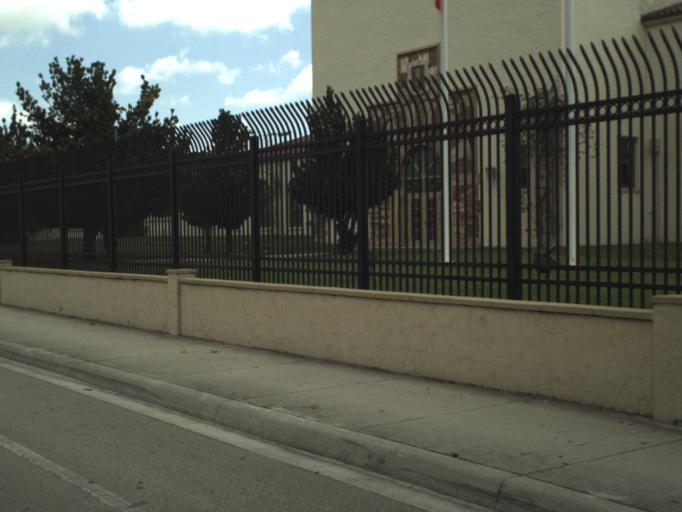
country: US
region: Florida
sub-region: Broward County
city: Broadview Park
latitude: 26.1018
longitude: -80.2012
